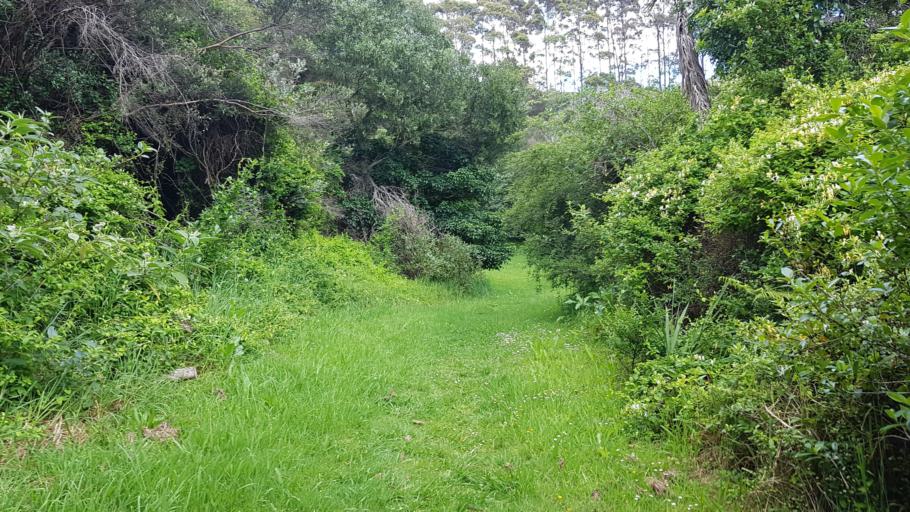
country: NZ
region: Auckland
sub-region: Auckland
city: Pakuranga
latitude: -36.7759
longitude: 175.0055
